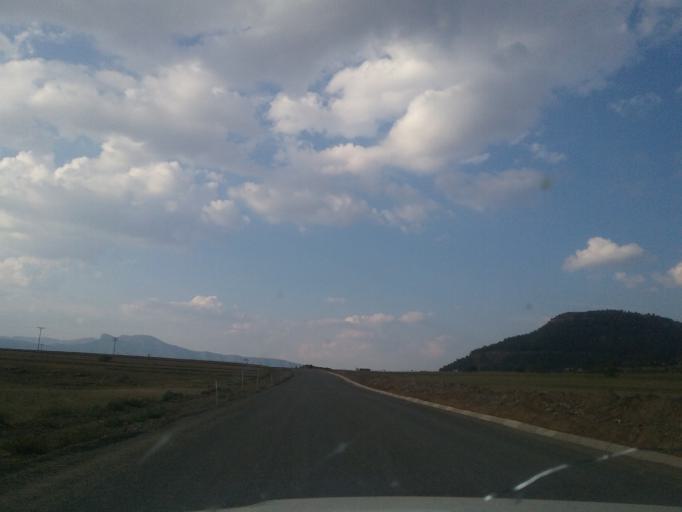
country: LS
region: Quthing
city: Quthing
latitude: -30.4056
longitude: 27.6077
